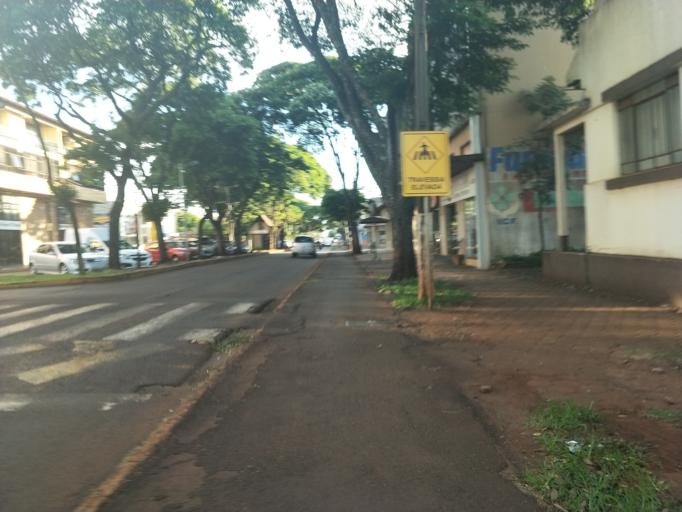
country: BR
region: Parana
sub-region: Marechal Candido Rondon
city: Marechal Candido Rondon
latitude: -24.5611
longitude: -54.0583
